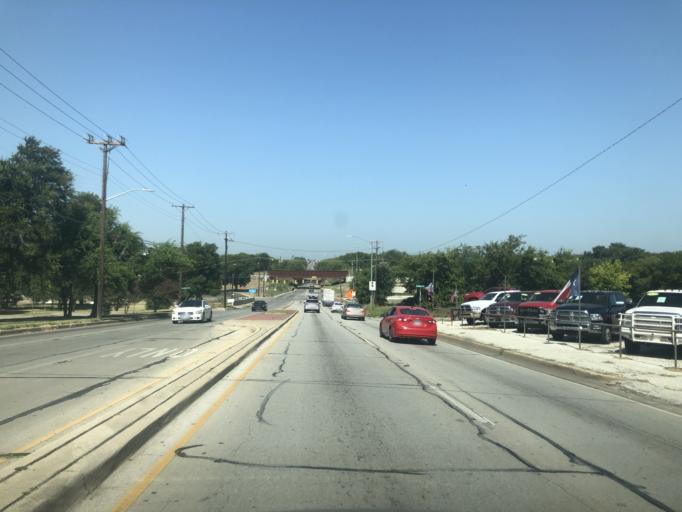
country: US
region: Texas
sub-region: Tarrant County
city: Blue Mound
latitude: 32.7952
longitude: -97.3351
